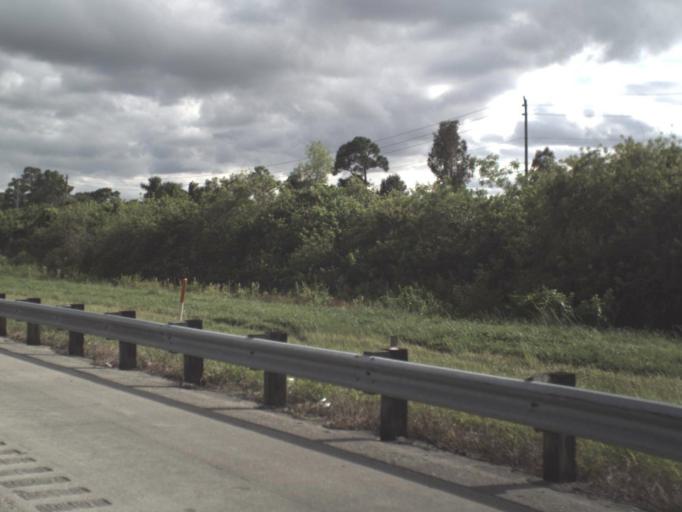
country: US
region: Florida
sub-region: Martin County
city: Palm City
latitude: 27.1037
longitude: -80.2642
